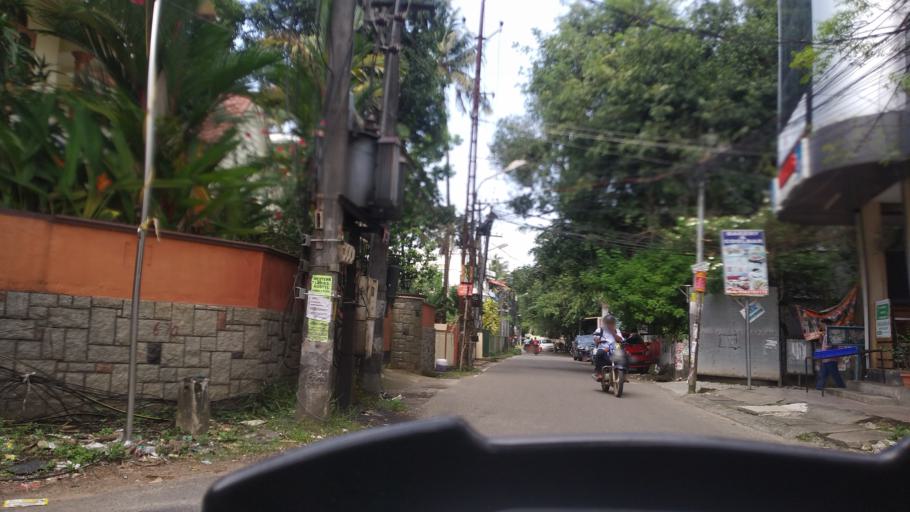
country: IN
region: Kerala
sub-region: Ernakulam
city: Cochin
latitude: 9.9909
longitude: 76.2970
